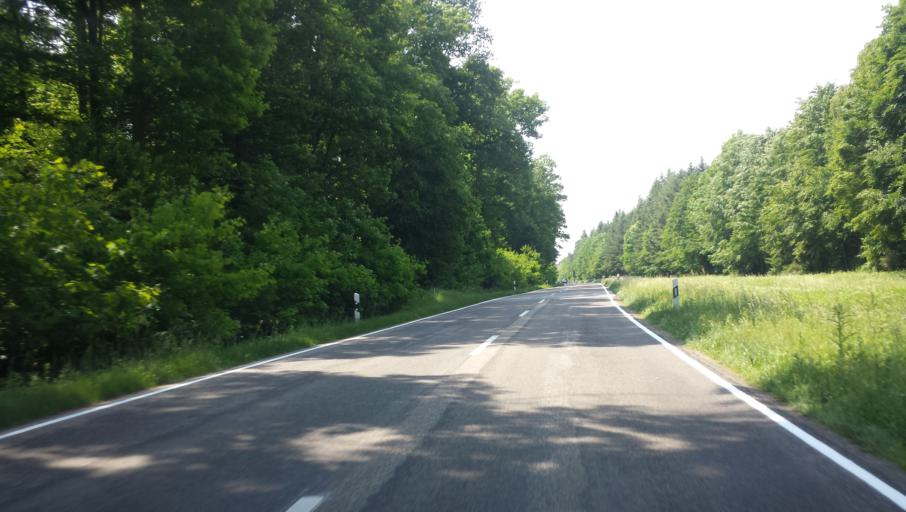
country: DE
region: Rheinland-Pfalz
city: Hagenbach
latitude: 49.0094
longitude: 8.2223
